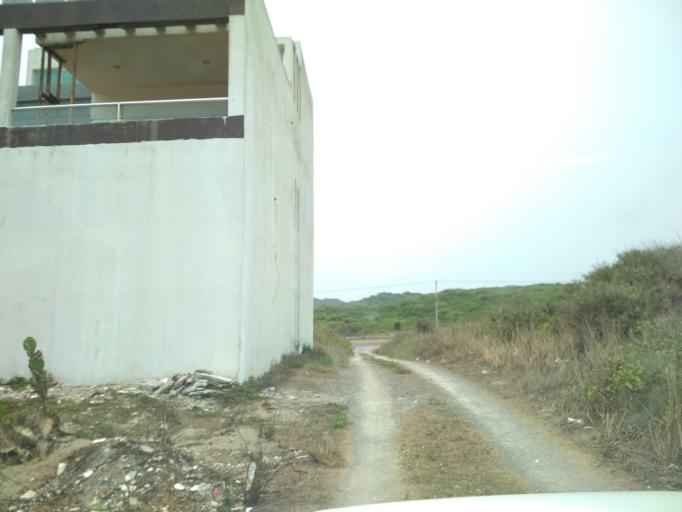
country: MX
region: Veracruz
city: Anton Lizardo
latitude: 19.0555
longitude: -96.0426
